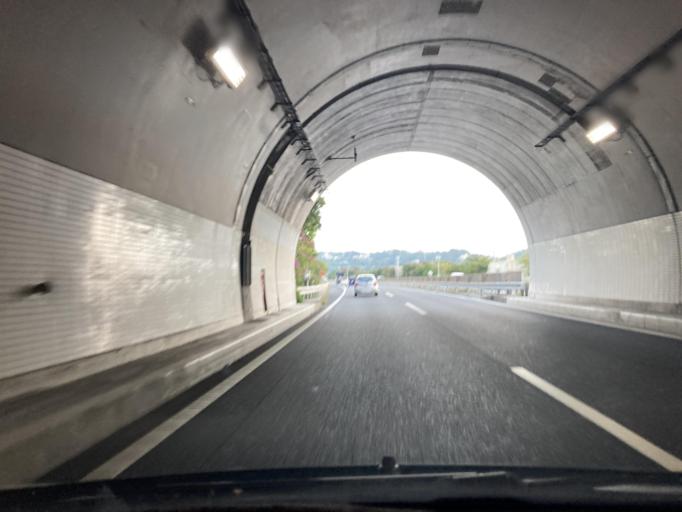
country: JP
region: Okinawa
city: Chatan
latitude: 26.3071
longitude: 127.7889
